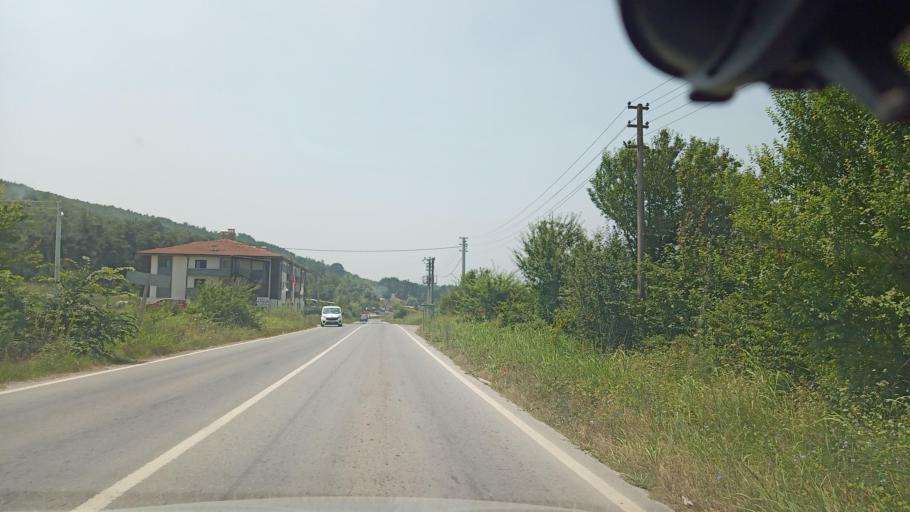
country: TR
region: Sakarya
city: Adapazari
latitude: 40.8362
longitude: 30.4089
